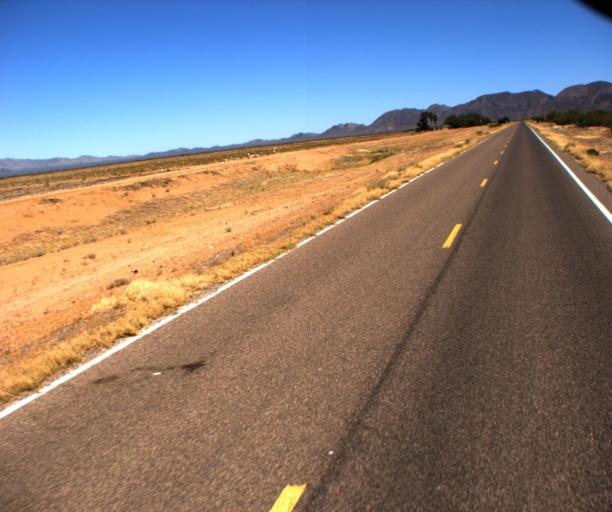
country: US
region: Arizona
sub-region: Yavapai County
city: Congress
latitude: 33.9638
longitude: -113.1415
